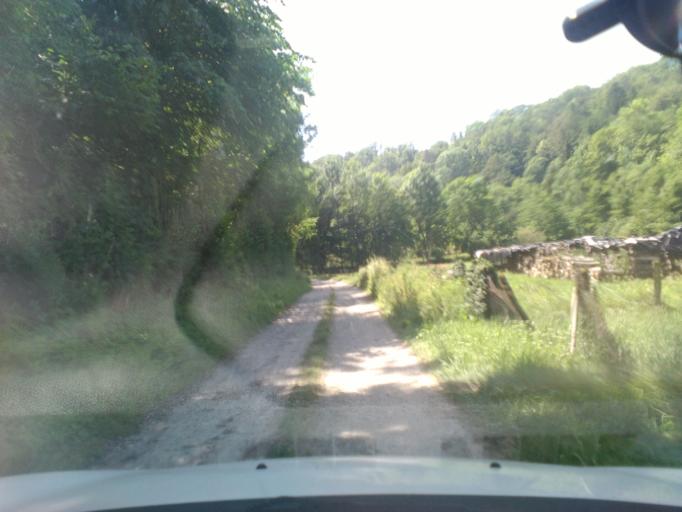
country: FR
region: Lorraine
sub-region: Departement des Vosges
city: Liffol-le-Grand
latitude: 48.3091
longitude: 5.3963
